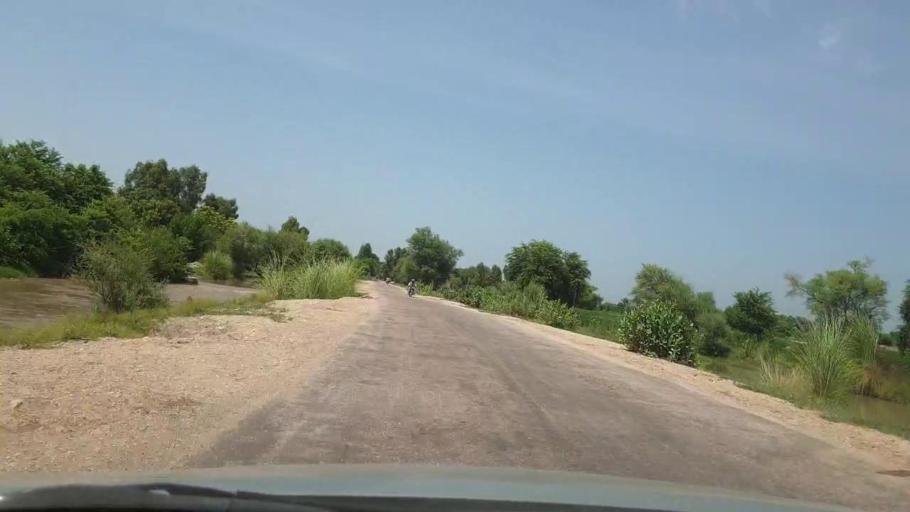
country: PK
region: Sindh
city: Pano Aqil
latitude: 27.6886
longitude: 69.1108
